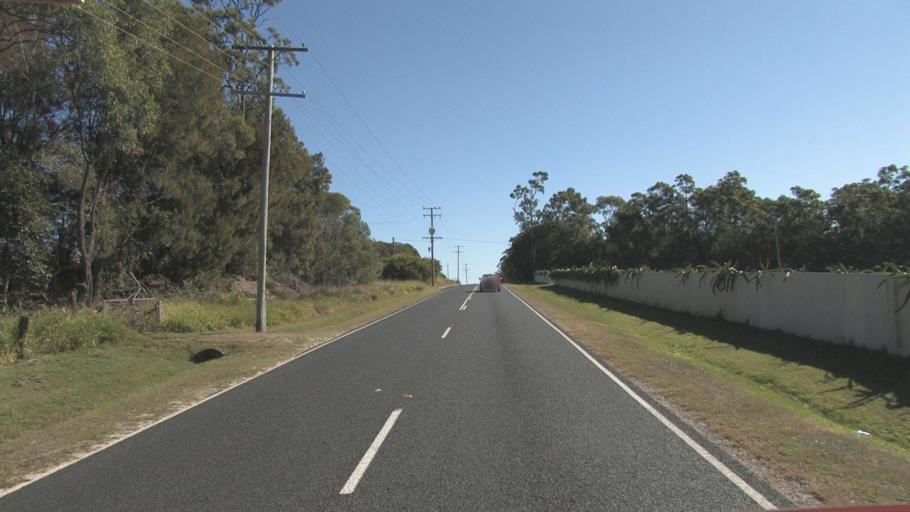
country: AU
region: Queensland
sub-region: Logan
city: Logan Reserve
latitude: -27.7204
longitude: 153.0786
